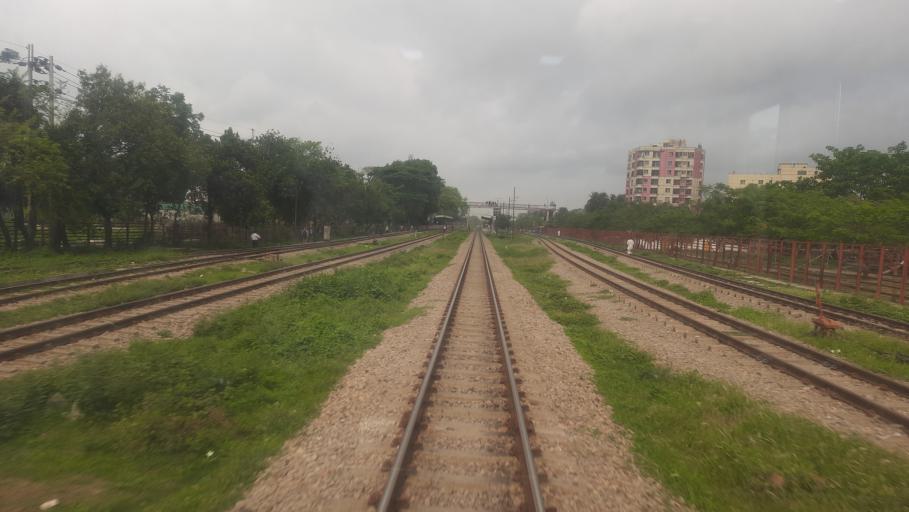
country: BD
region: Dhaka
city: Narsingdi
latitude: 23.9312
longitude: 90.7239
